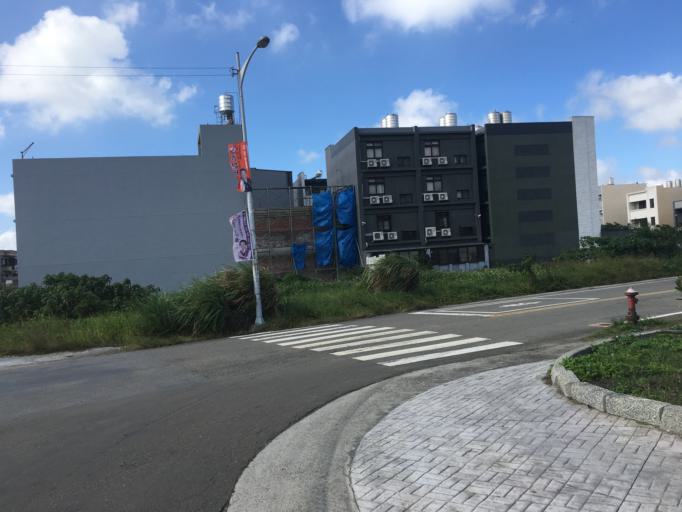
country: TW
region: Taiwan
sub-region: Hsinchu
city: Zhubei
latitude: 24.8938
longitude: 121.0454
